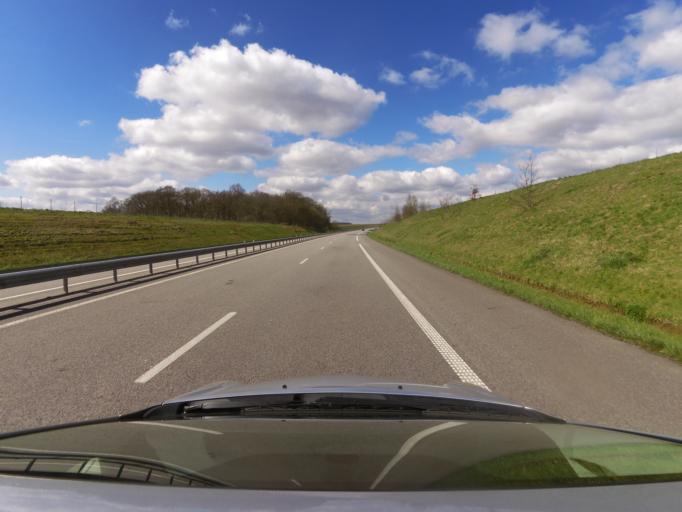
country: FR
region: Haute-Normandie
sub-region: Departement de la Seine-Maritime
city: Limesy
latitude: 49.6452
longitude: 0.9681
